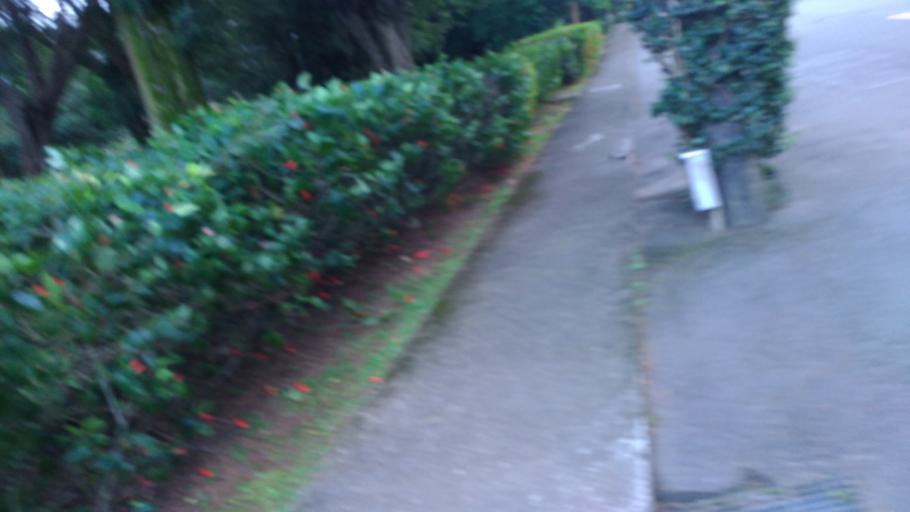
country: TW
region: Taiwan
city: Daxi
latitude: 24.8883
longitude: 121.1706
